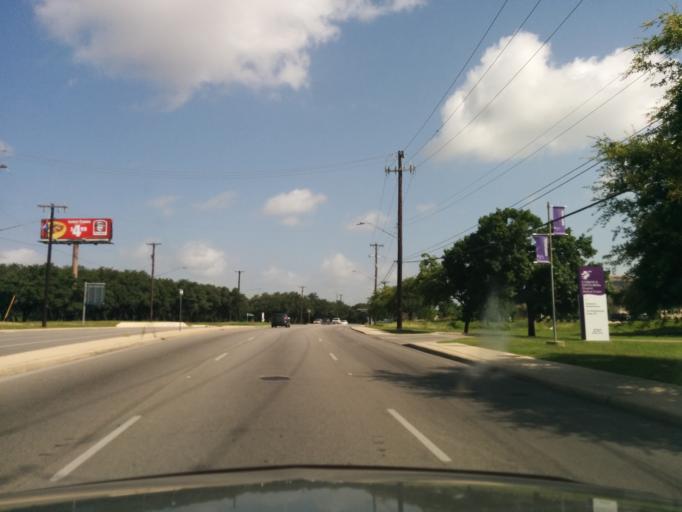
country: US
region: Texas
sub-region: Bexar County
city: Leon Valley
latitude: 29.5097
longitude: -98.5904
